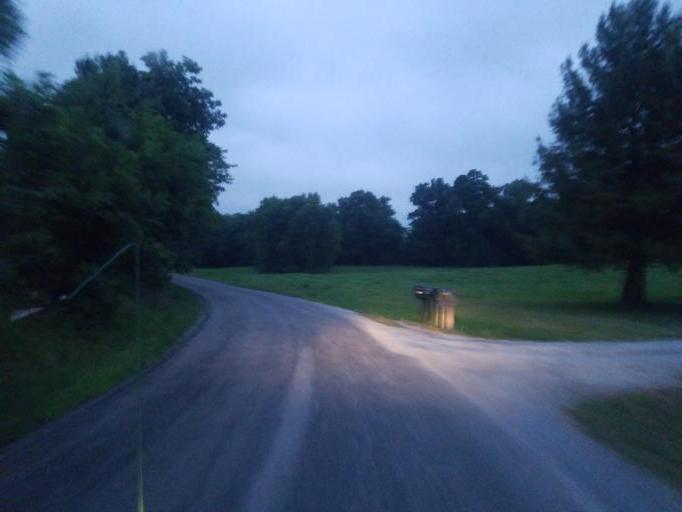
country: US
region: Illinois
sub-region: Jackson County
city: Murphysboro
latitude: 37.6860
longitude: -89.3133
